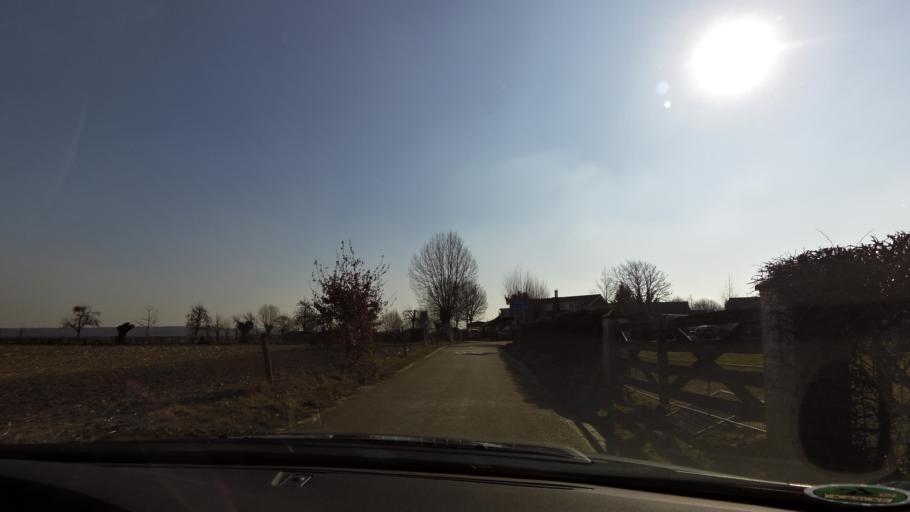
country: BE
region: Flanders
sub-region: Provincie Limburg
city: Sint-Pieters-Voeren
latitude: 50.7764
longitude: 5.8911
